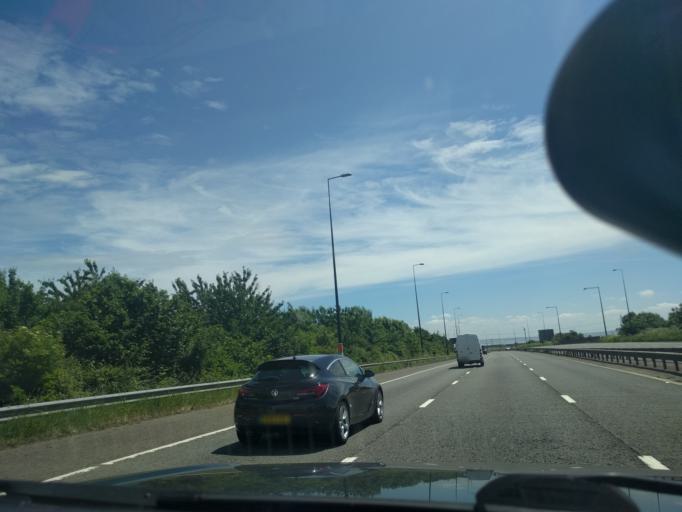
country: GB
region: Wales
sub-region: Monmouthshire
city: Rogiet
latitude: 51.5848
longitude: -2.7981
